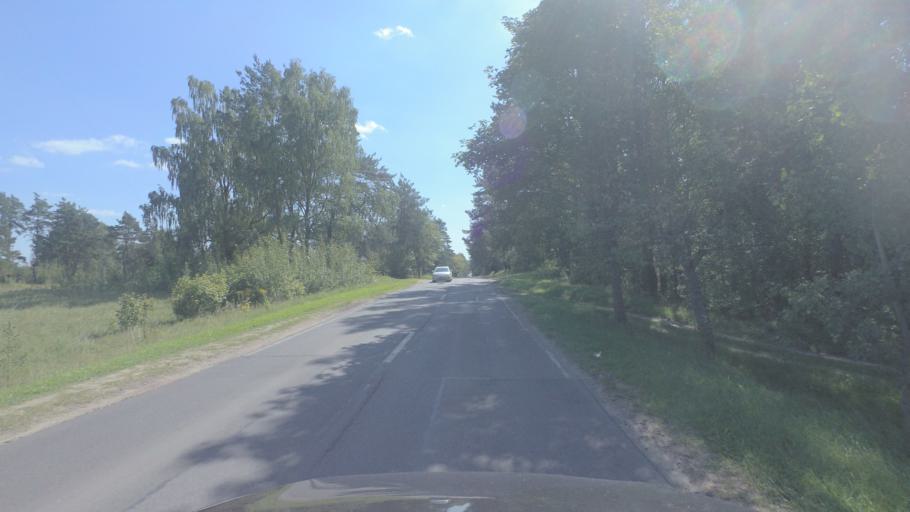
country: LT
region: Vilnius County
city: Rasos
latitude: 54.7977
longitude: 25.3493
